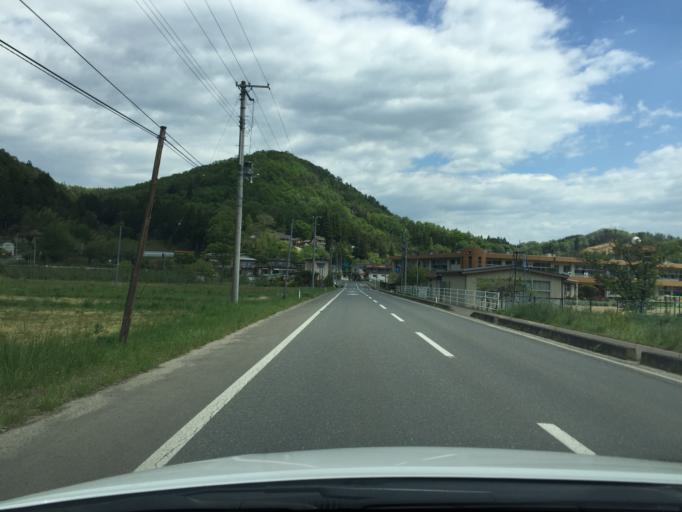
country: JP
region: Fukushima
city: Hobaramachi
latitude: 37.7661
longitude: 140.5781
